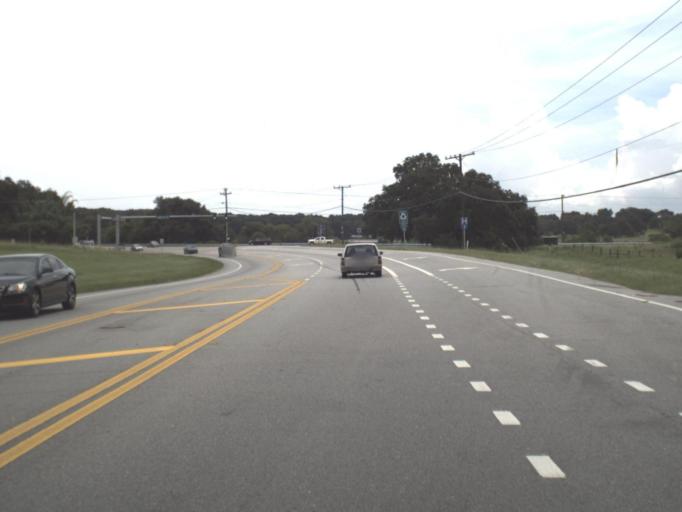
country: US
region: Florida
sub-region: Pasco County
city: Saint Leo
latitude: 28.3356
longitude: -82.2393
